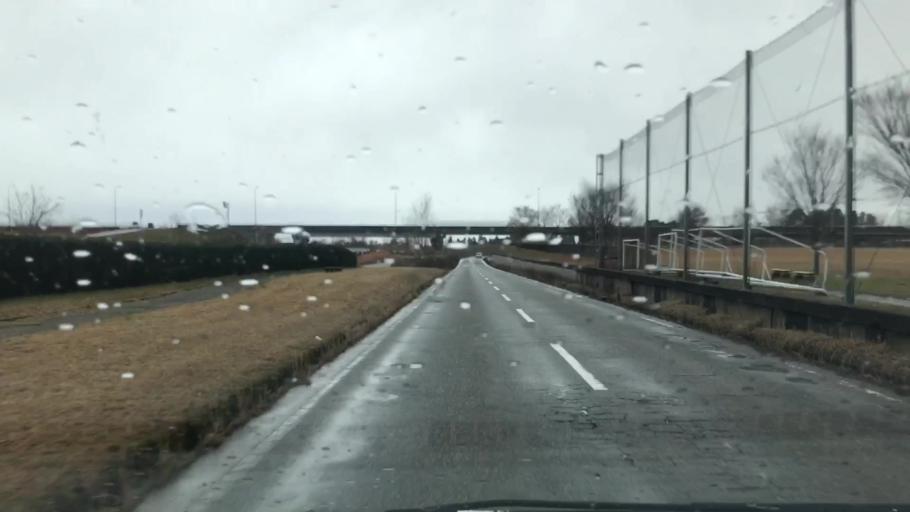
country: JP
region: Toyama
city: Kamiichi
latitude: 36.6251
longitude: 137.3014
